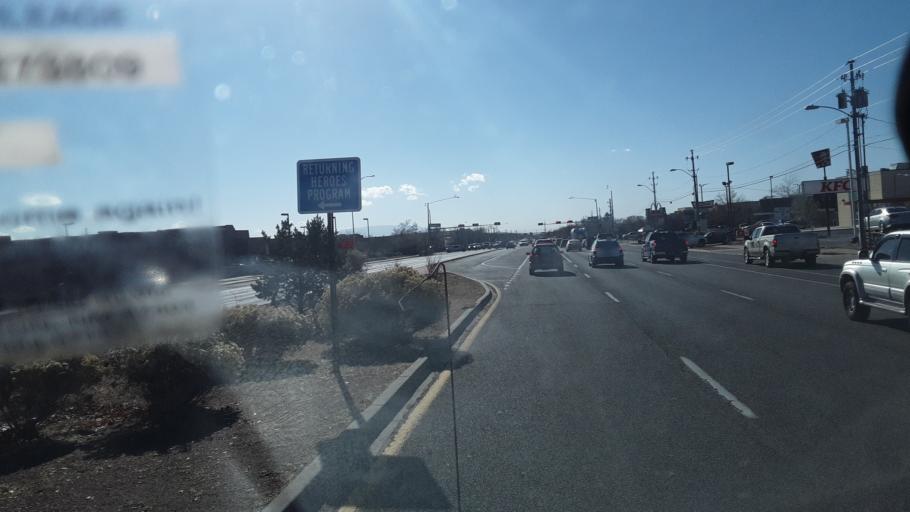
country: US
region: New Mexico
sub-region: Santa Fe County
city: Agua Fria
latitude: 35.6506
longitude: -105.9996
